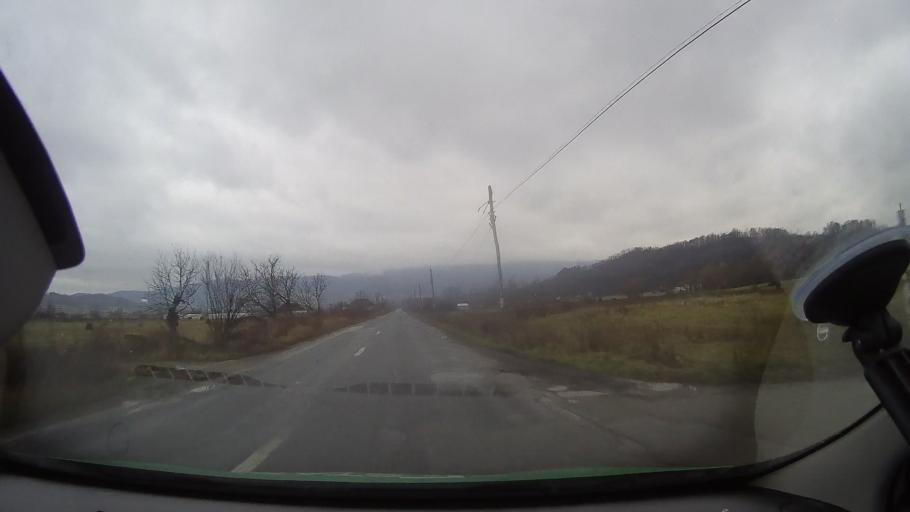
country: RO
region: Arad
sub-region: Comuna Halmagiu
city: Halmagiu
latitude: 46.2631
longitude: 22.5896
